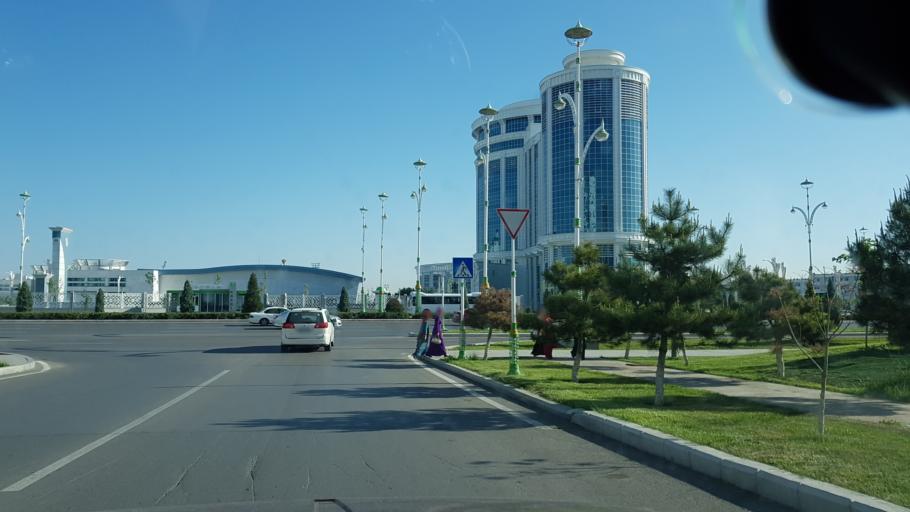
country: TM
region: Ahal
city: Ashgabat
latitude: 37.8949
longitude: 58.3771
